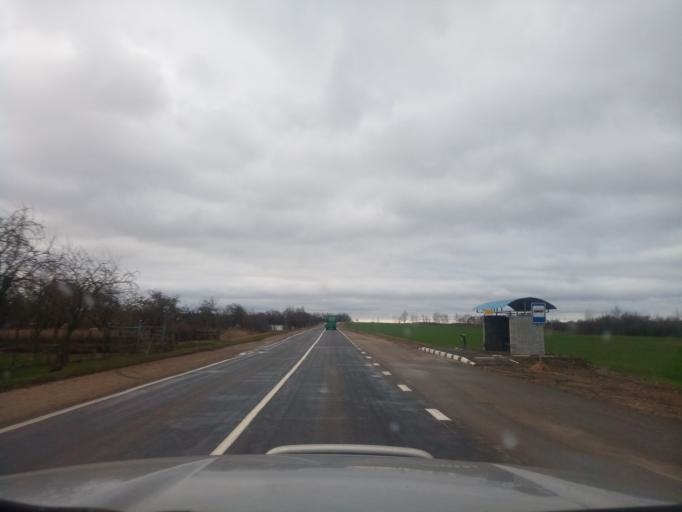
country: BY
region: Minsk
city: Kapyl'
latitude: 53.1755
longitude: 27.1640
